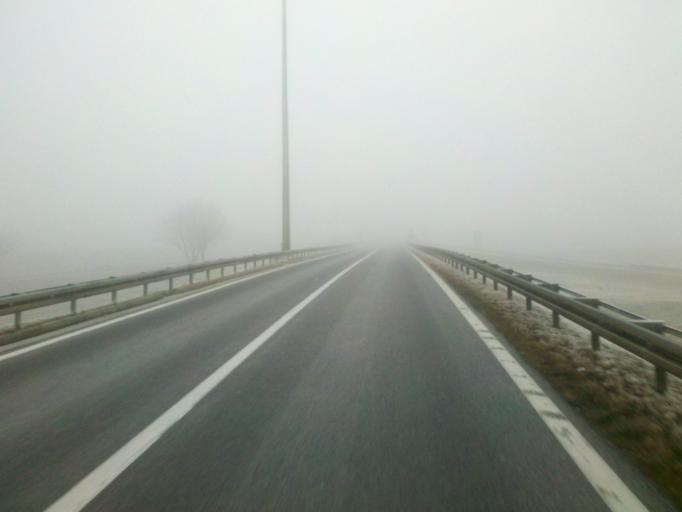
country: HR
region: Medimurska
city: Kursanec
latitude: 46.2611
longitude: 16.4003
